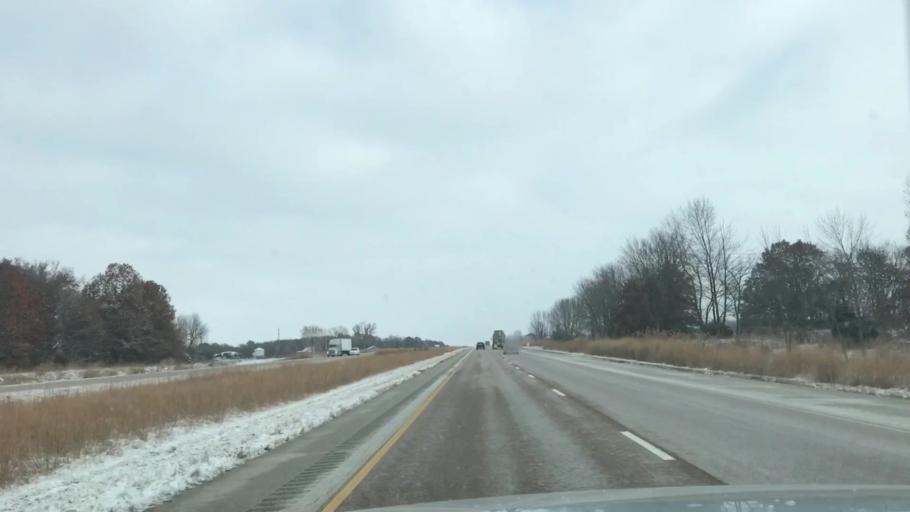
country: US
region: Illinois
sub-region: Macoupin County
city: Mount Olive
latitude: 39.1031
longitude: -89.7324
